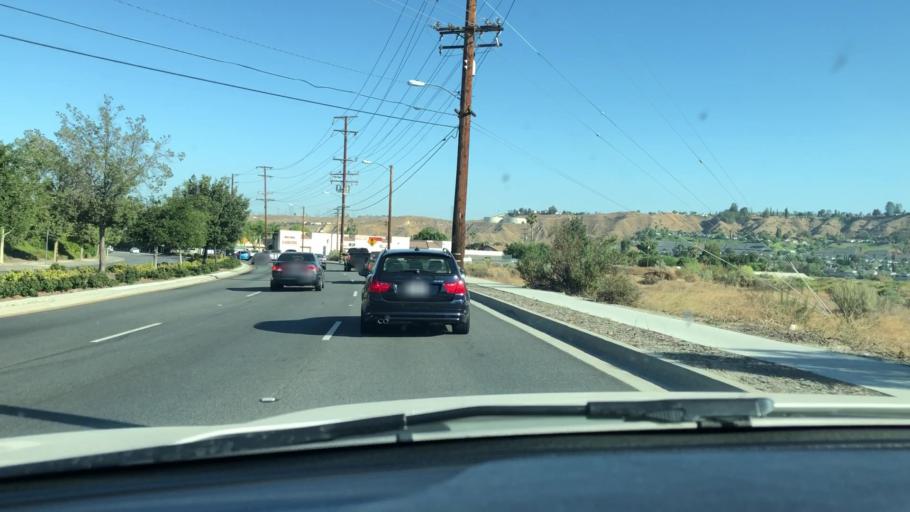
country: US
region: California
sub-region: Los Angeles County
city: Santa Clarita
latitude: 34.4196
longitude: -118.4826
